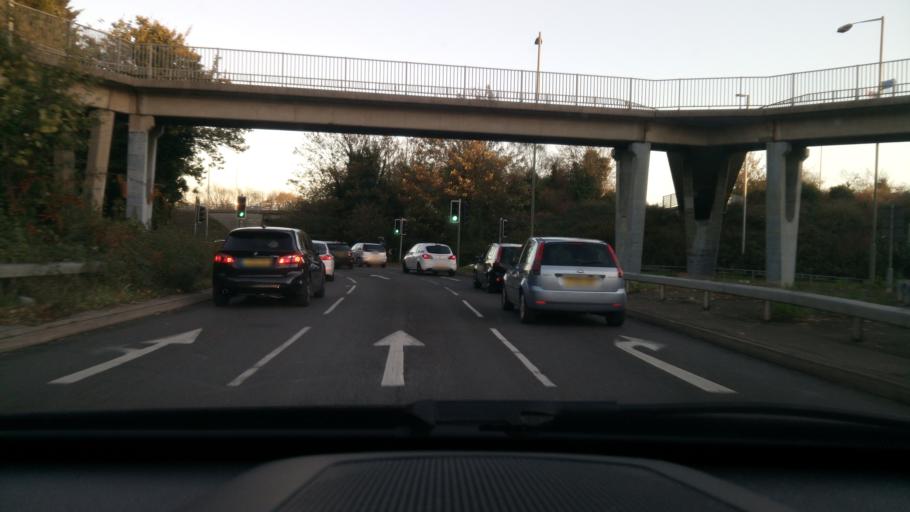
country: GB
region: England
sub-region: Peterborough
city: Peterborough
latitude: 52.5993
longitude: -0.2629
